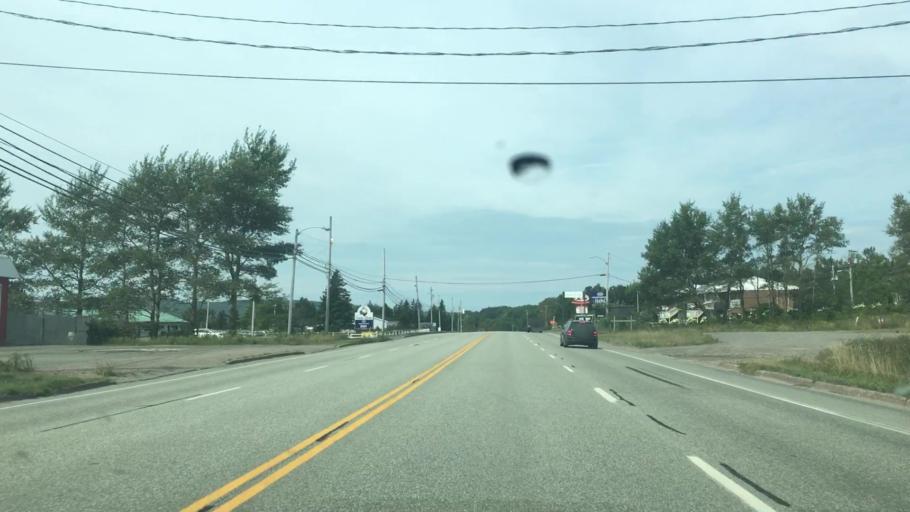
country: CA
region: Nova Scotia
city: Port Hawkesbury
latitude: 45.6408
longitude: -61.3883
